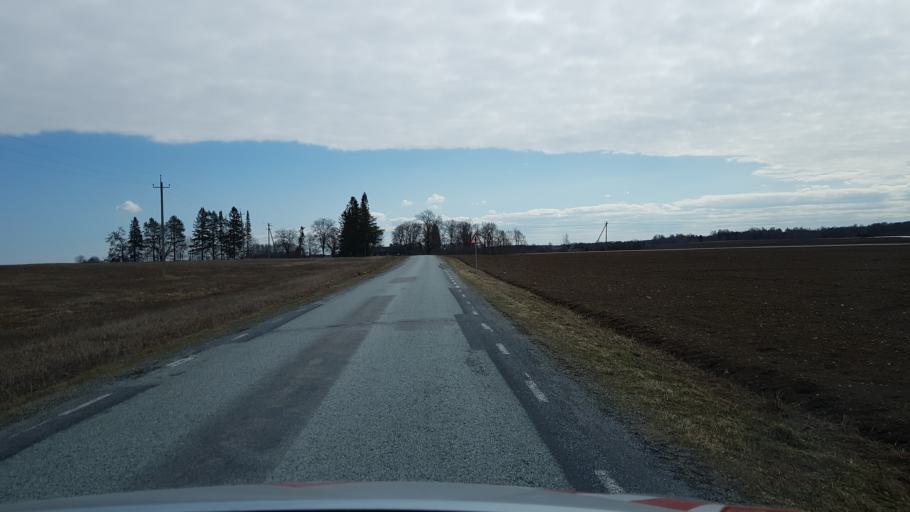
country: EE
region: Laeaene-Virumaa
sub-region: Haljala vald
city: Haljala
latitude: 59.4254
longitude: 26.2230
